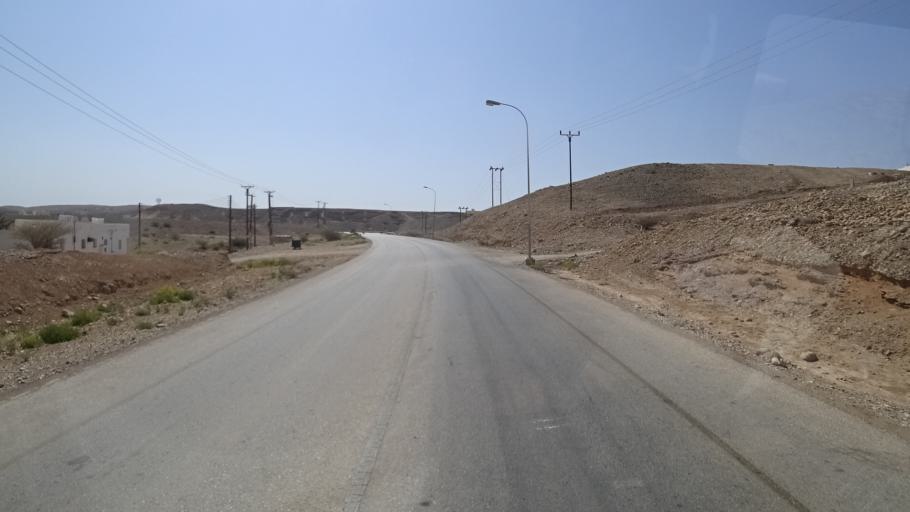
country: OM
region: Ash Sharqiyah
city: Sur
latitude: 22.5432
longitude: 59.5026
